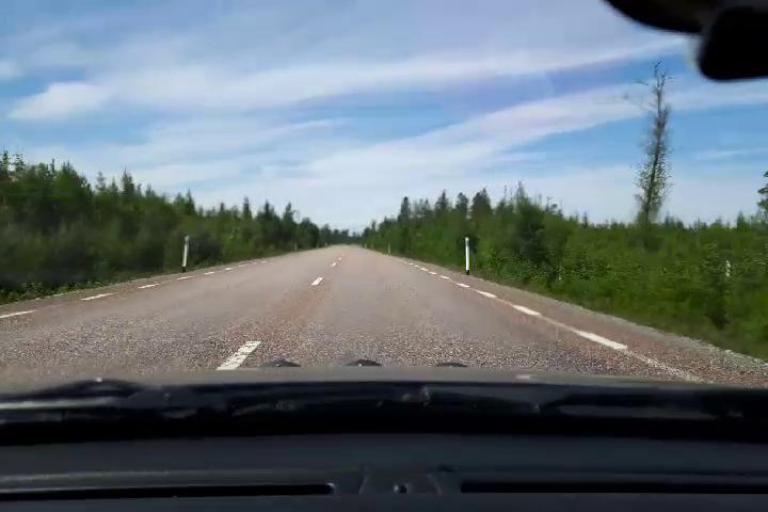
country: SE
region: Gaevleborg
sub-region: Gavle Kommun
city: Norrsundet
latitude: 61.0818
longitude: 16.9612
